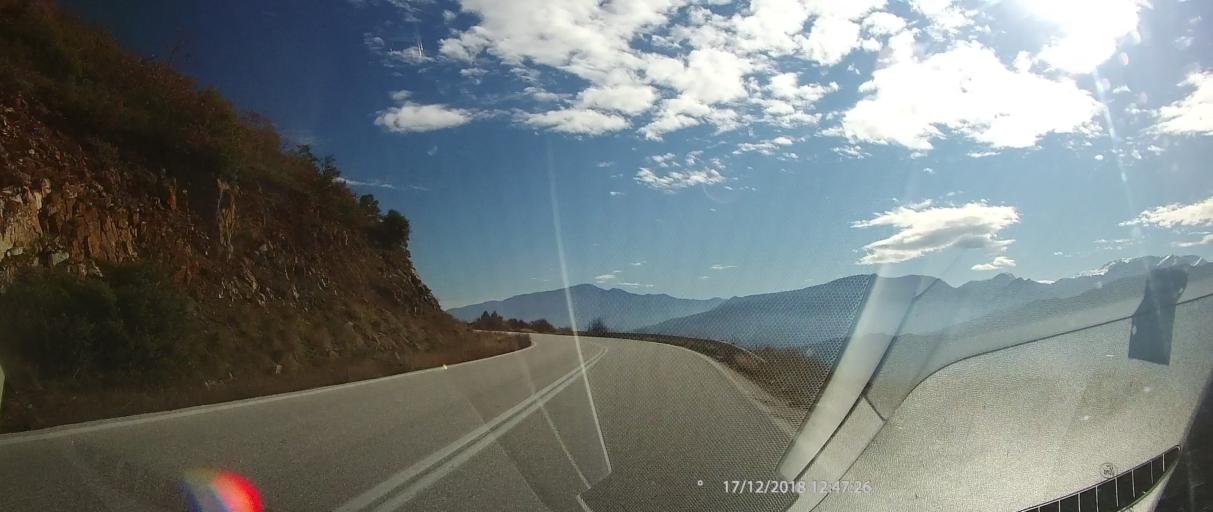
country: GR
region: Thessaly
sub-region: Trikala
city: Kastraki
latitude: 39.7852
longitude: 21.4284
